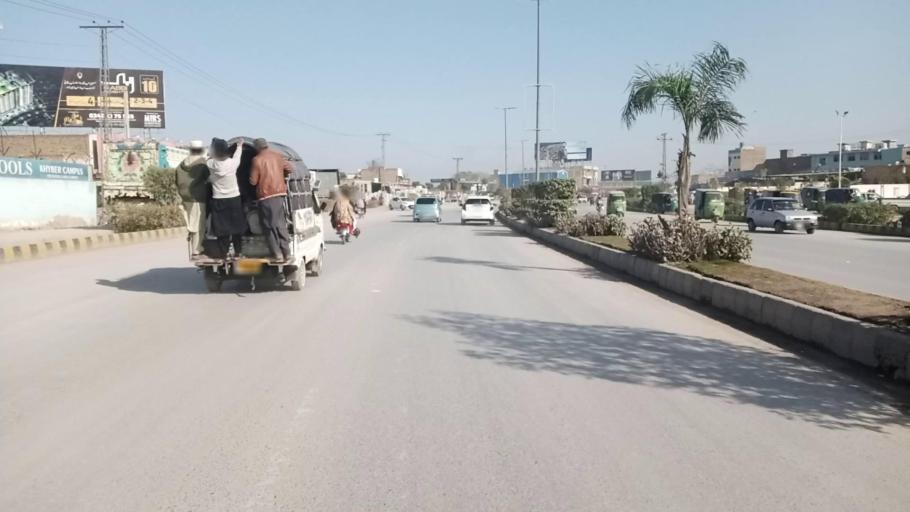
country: PK
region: Khyber Pakhtunkhwa
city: Peshawar
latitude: 34.0336
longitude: 71.6017
